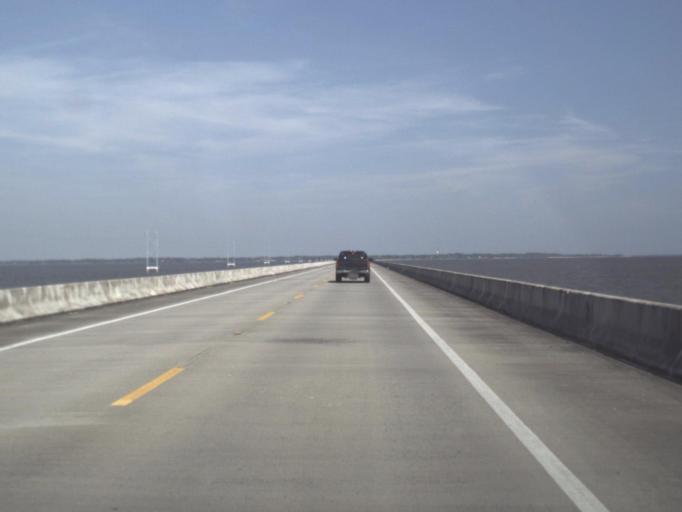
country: US
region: Florida
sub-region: Franklin County
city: Apalachicola
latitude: 29.7286
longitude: -84.9513
